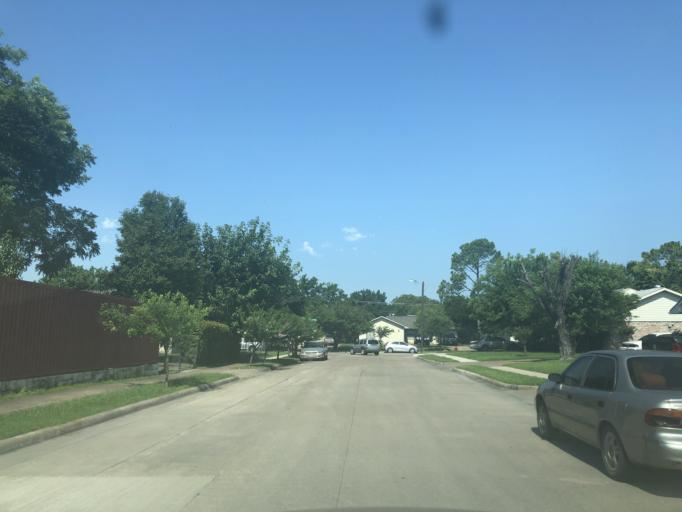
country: US
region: Texas
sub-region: Dallas County
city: Grand Prairie
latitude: 32.7232
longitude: -97.0007
